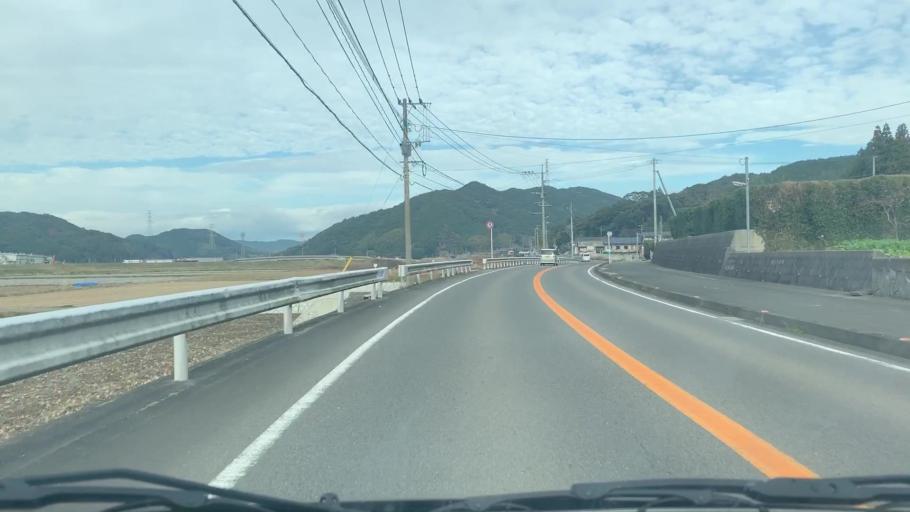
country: JP
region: Saga Prefecture
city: Karatsu
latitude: 33.3689
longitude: 130.0042
